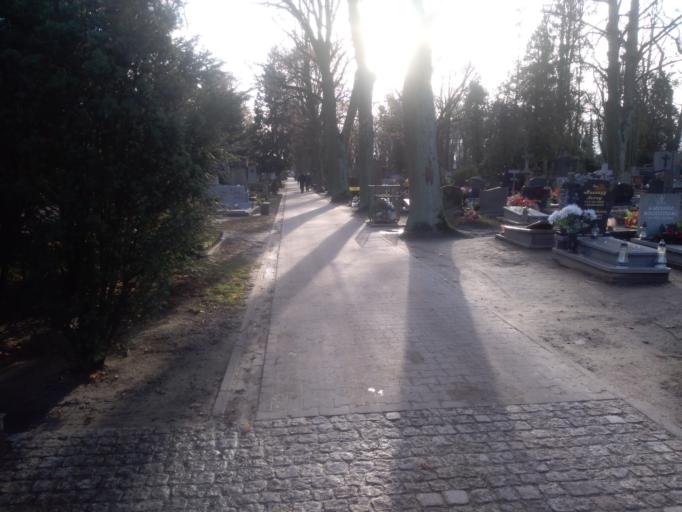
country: PL
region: Greater Poland Voivodeship
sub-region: Poznan
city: Poznan
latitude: 52.4159
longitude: 16.8791
